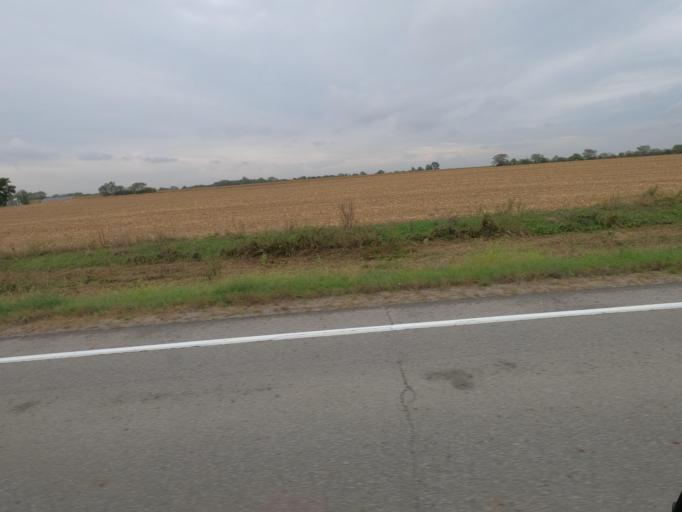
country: US
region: Iowa
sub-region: Van Buren County
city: Keosauqua
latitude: 40.8134
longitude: -91.9077
